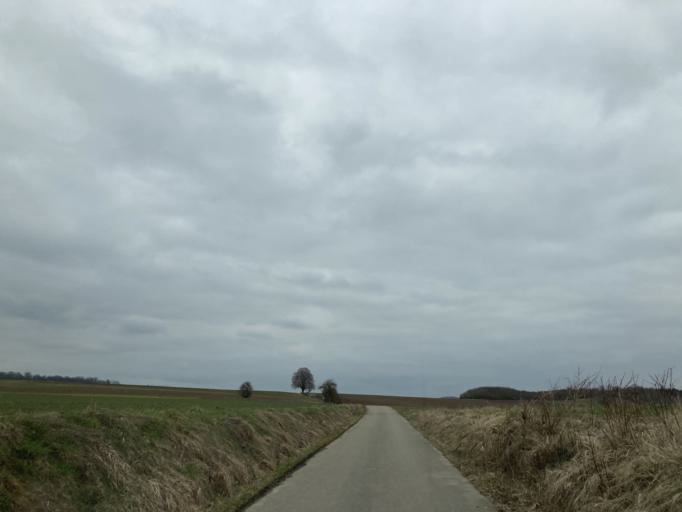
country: DE
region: Baden-Wuerttemberg
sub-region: Tuebingen Region
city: Hirrlingen
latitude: 48.4193
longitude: 8.8962
